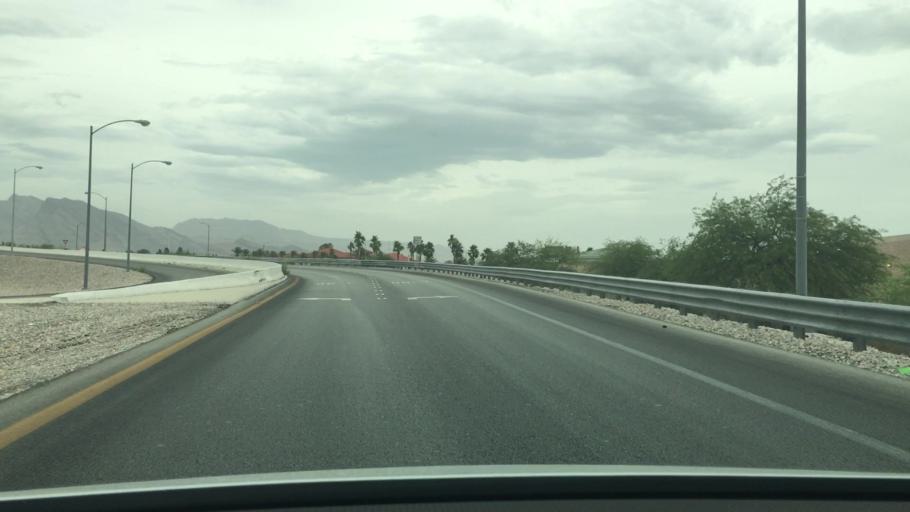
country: US
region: Nevada
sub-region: Clark County
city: Spring Valley
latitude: 36.1796
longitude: -115.2581
